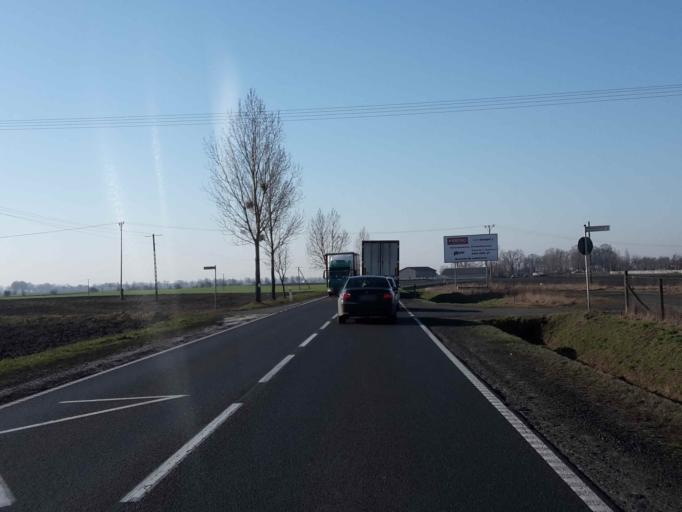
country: PL
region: Kujawsko-Pomorskie
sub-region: Powiat inowroclawski
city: Wierzchoslawice
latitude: 52.8551
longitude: 18.3490
